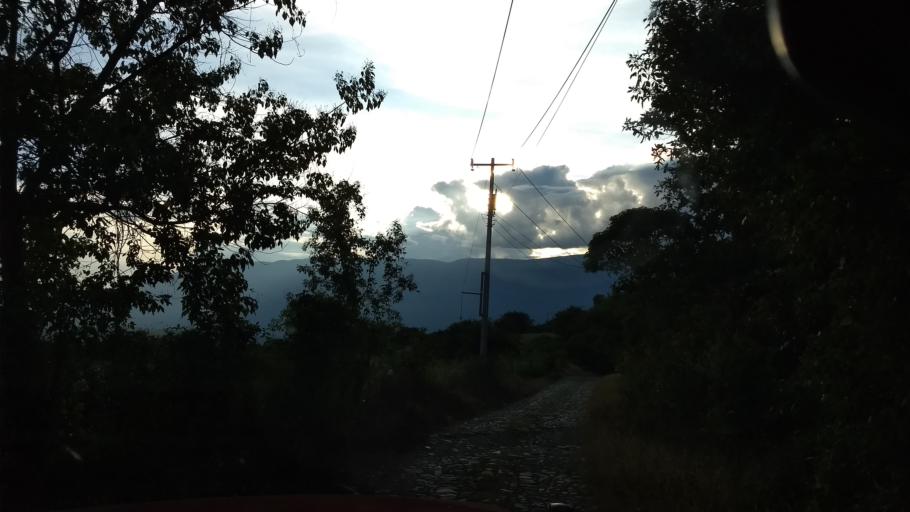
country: MX
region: Jalisco
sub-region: San Gabriel
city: Alista
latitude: 19.5072
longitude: -103.7535
